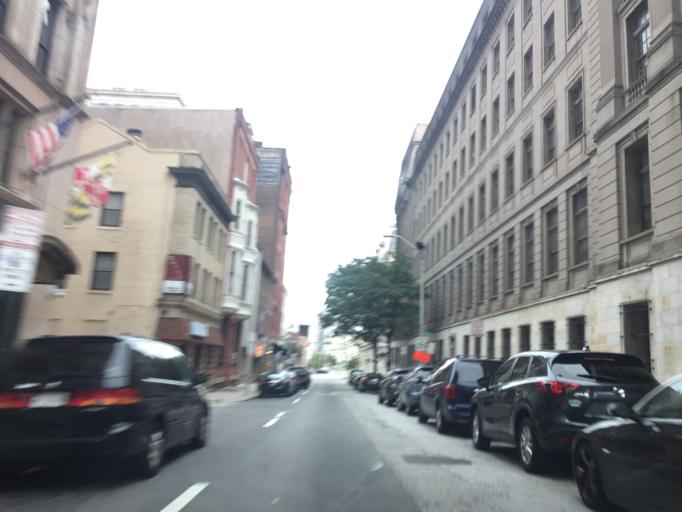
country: US
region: Maryland
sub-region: City of Baltimore
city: Baltimore
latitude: 39.2912
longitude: -76.6123
